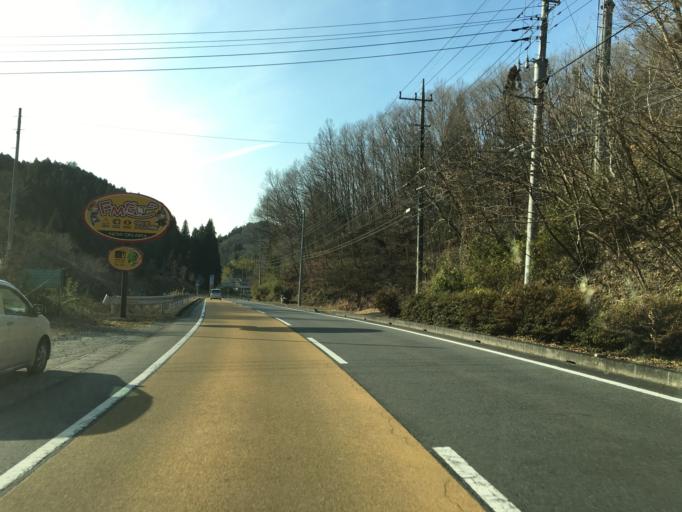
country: JP
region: Ibaraki
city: Daigo
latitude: 36.7496
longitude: 140.4510
